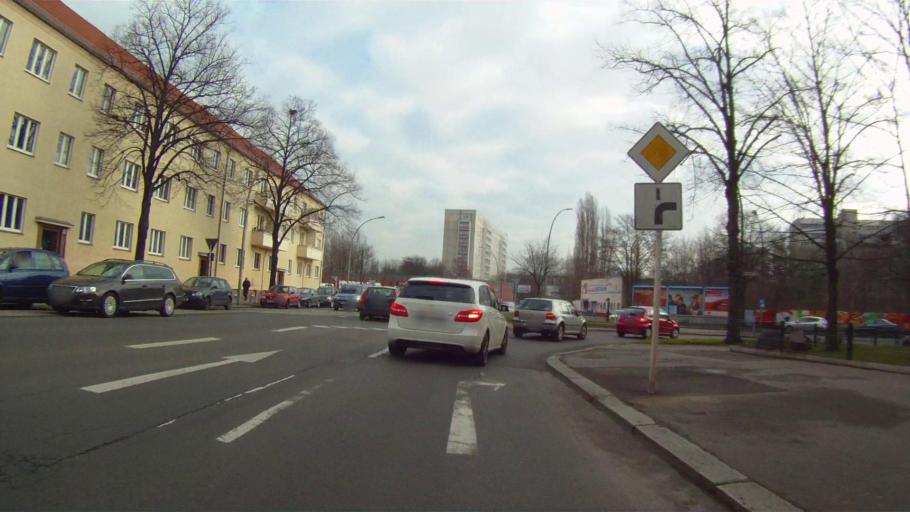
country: DE
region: Berlin
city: Lichtenberg
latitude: 52.5123
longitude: 13.5058
